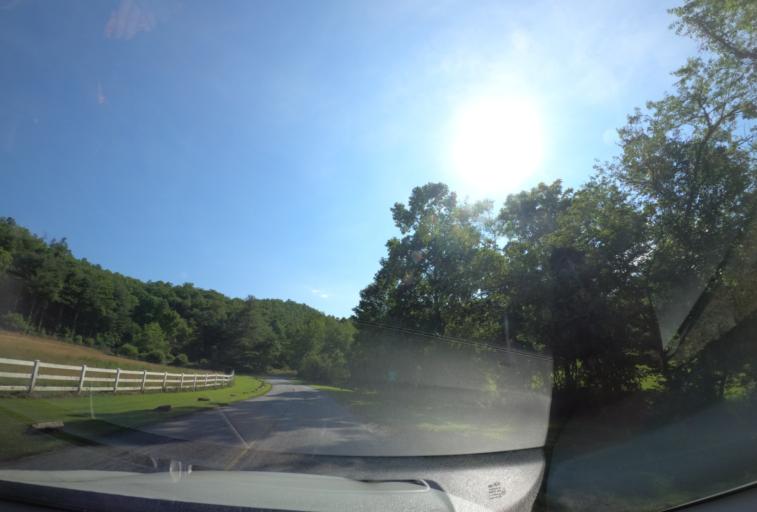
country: US
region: North Carolina
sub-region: Transylvania County
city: Brevard
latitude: 35.2260
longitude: -82.6442
